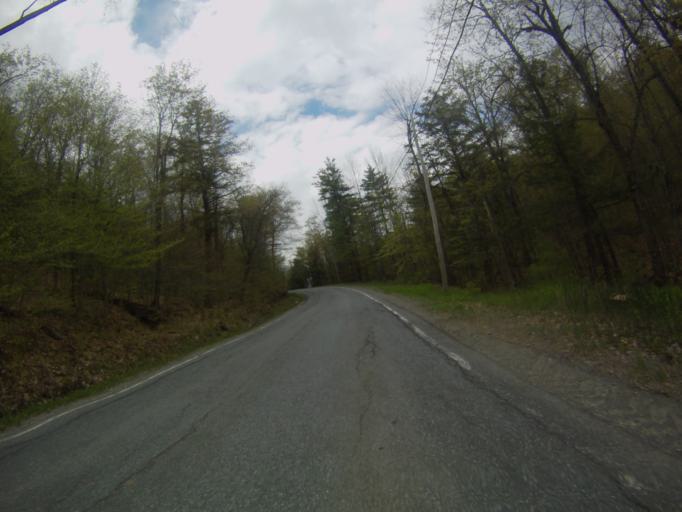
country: US
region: New York
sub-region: Essex County
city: Port Henry
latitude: 43.9837
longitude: -73.4900
